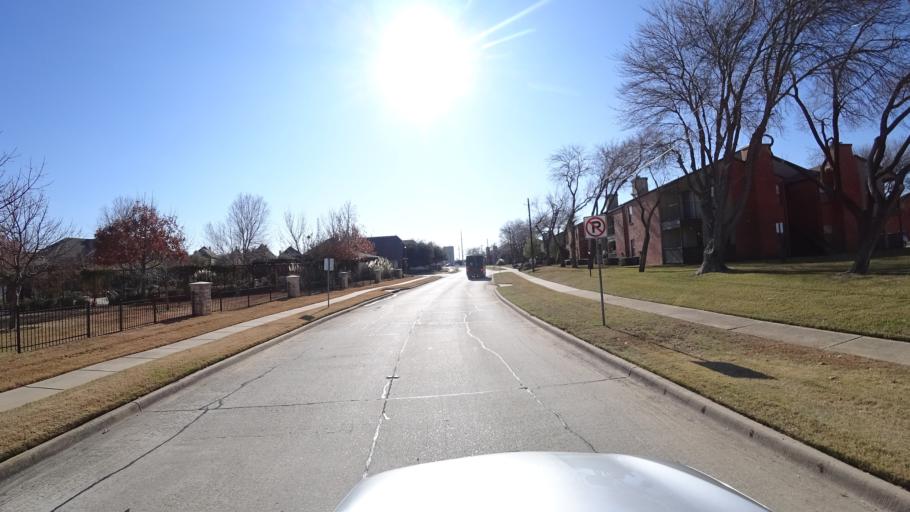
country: US
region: Texas
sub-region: Denton County
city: Lewisville
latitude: 33.0058
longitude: -96.9975
